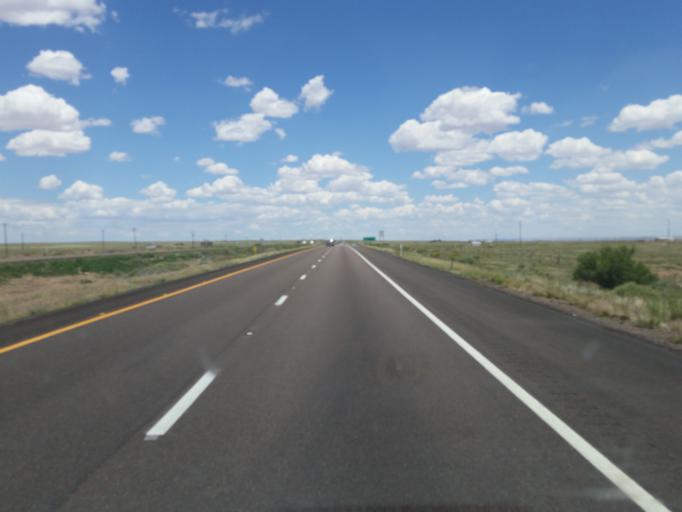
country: US
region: Arizona
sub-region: Navajo County
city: Holbrook
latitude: 34.9826
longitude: -110.0433
